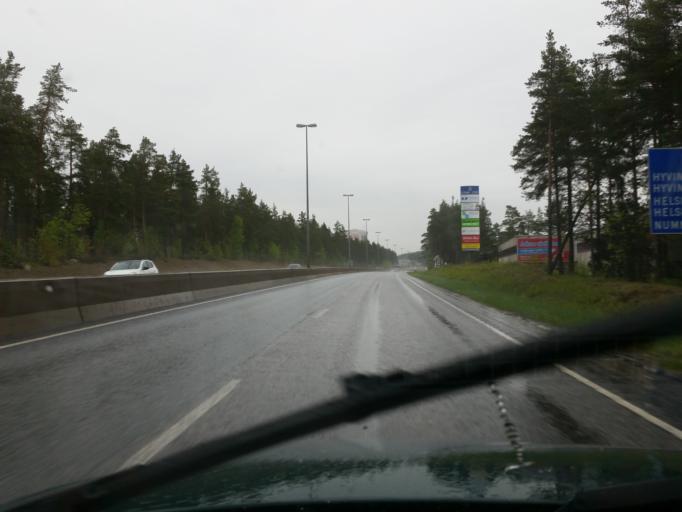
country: FI
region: Uusimaa
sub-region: Helsinki
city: Lohja
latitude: 60.2639
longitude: 24.1071
